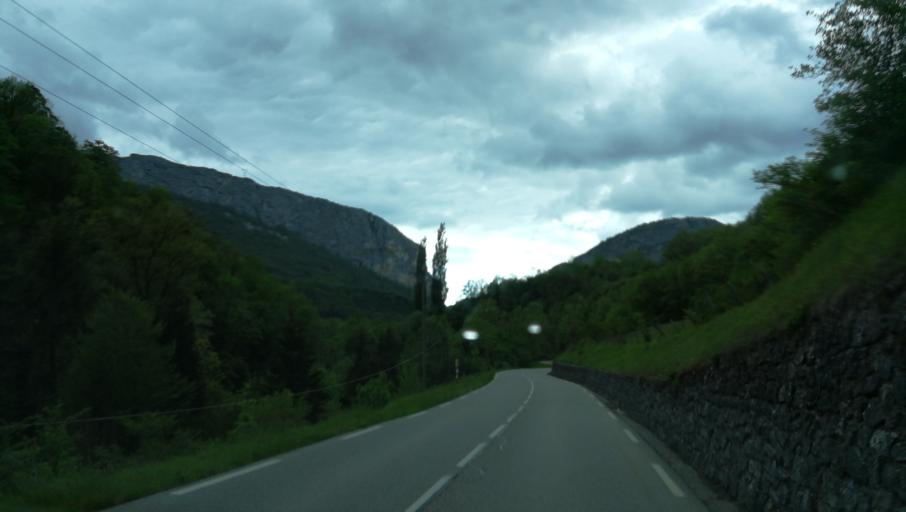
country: FR
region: Rhone-Alpes
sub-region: Departement de l'Isere
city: Pont-en-Royans
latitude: 45.0673
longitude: 5.3796
